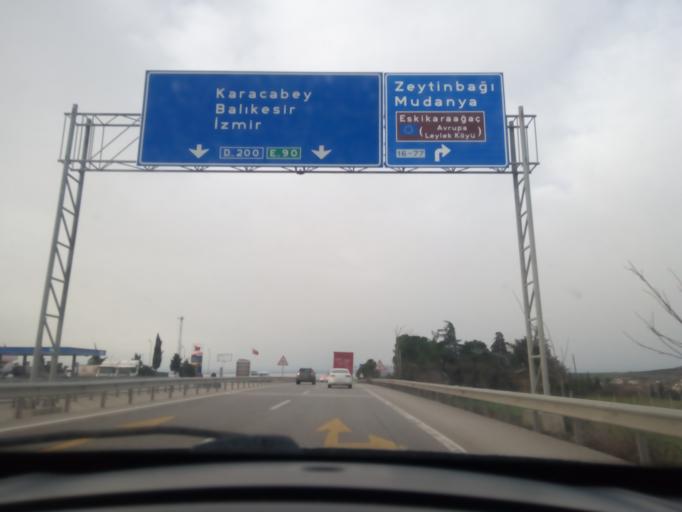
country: TR
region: Bursa
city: Mahmudiye
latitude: 40.2161
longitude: 28.6277
